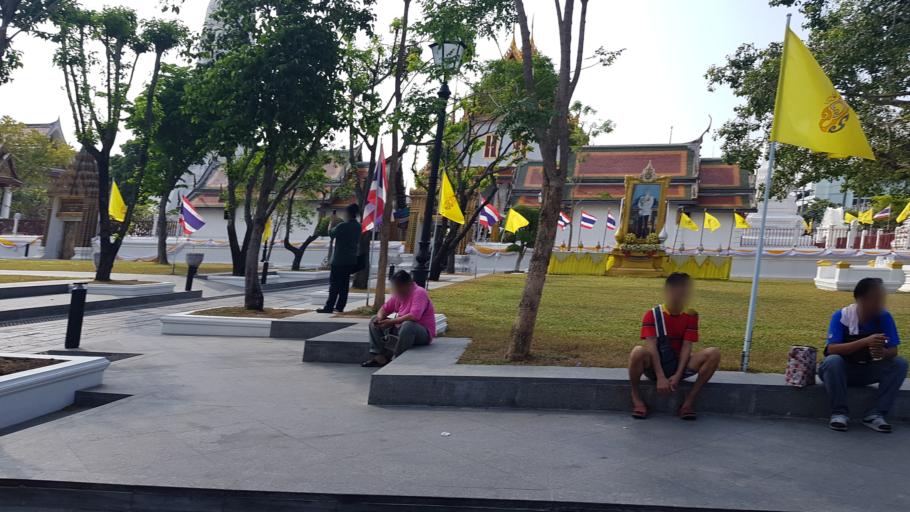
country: TH
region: Bangkok
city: Bangkok Noi
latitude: 13.7527
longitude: 100.4862
